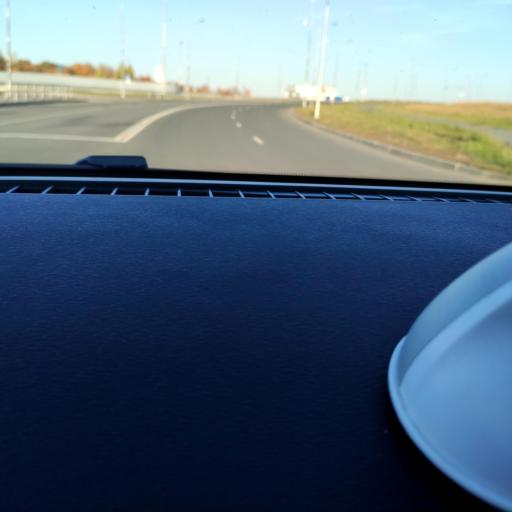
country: RU
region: Samara
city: Samara
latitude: 53.2903
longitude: 50.2288
